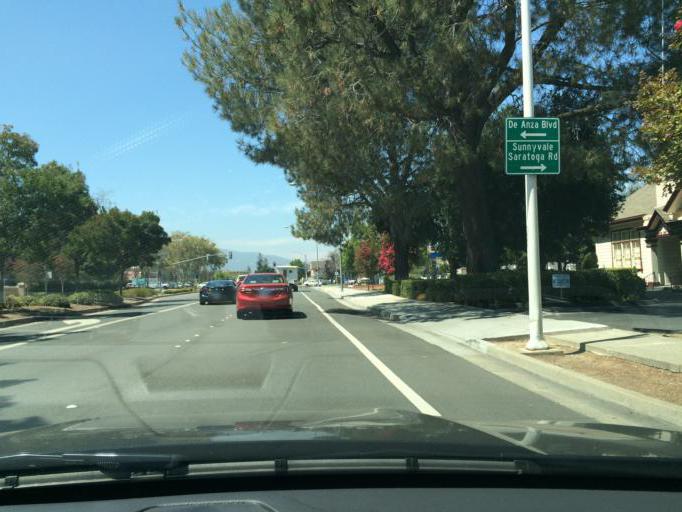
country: US
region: California
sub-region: Santa Clara County
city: Cupertino
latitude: 37.3377
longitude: -122.0305
